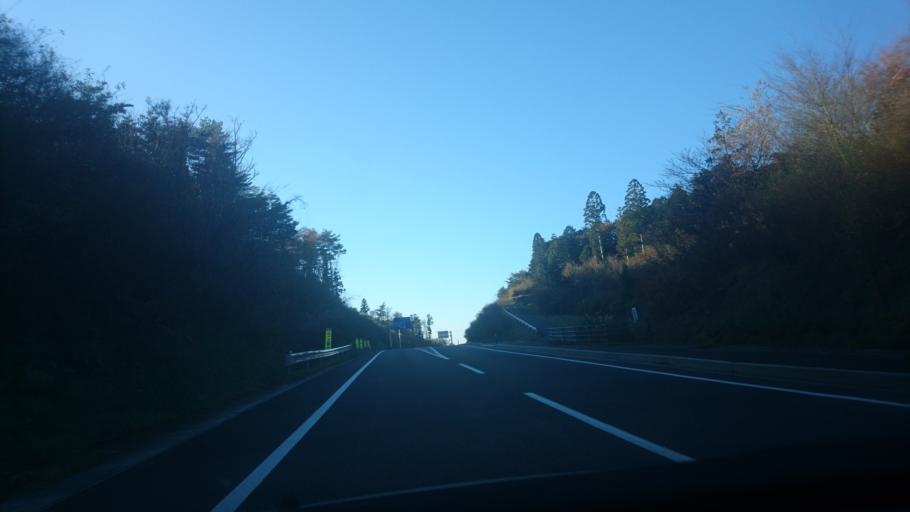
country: JP
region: Iwate
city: Ichinoseki
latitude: 38.9040
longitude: 141.1752
